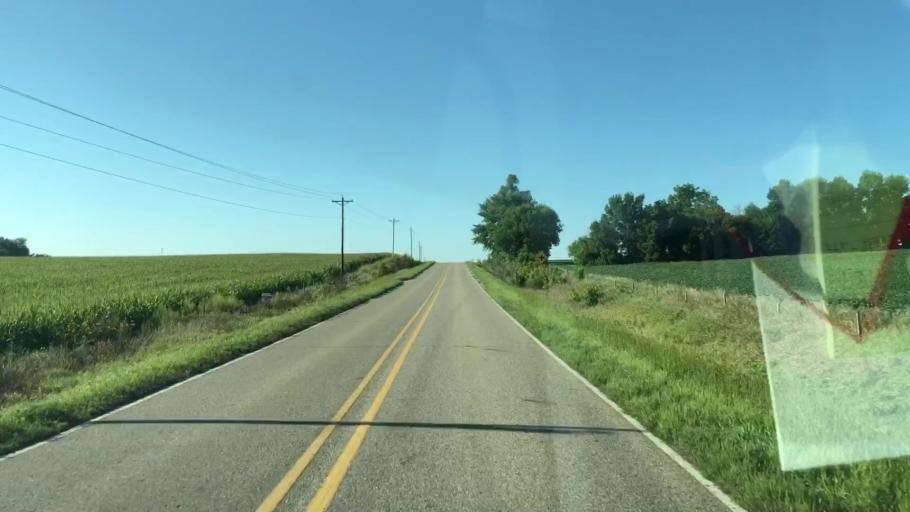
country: US
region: Iowa
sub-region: Woodbury County
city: Moville
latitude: 42.4630
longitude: -96.2138
